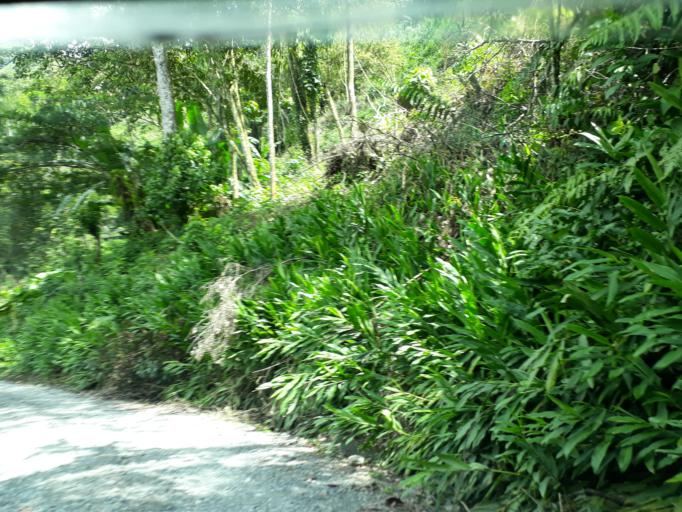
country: CO
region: Cundinamarca
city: Topaipi
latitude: 5.3482
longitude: -74.1991
